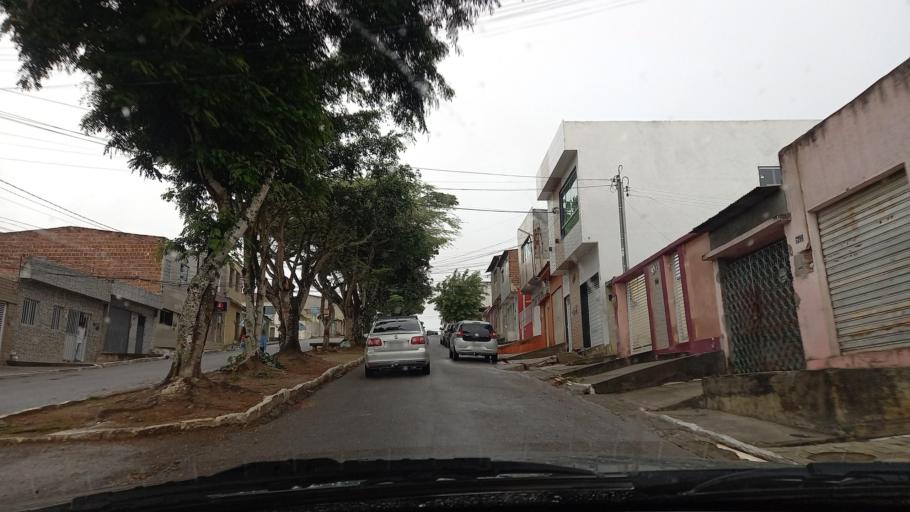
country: BR
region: Pernambuco
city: Garanhuns
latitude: -8.8801
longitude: -36.4985
